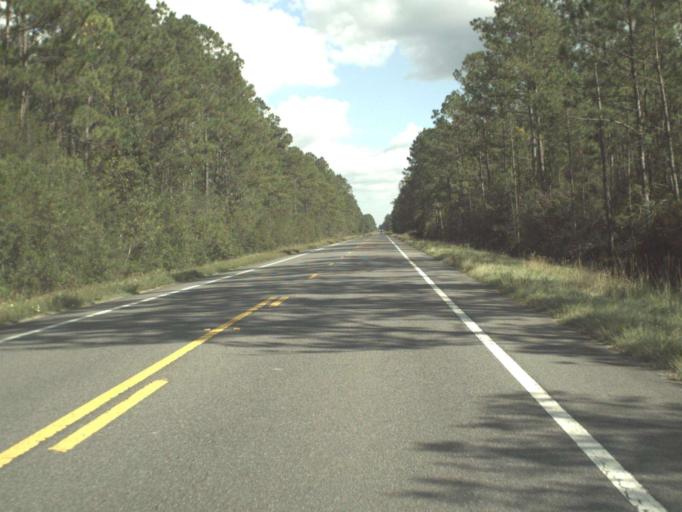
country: US
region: Florida
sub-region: Bay County
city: Laguna Beach
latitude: 30.4470
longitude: -85.8376
